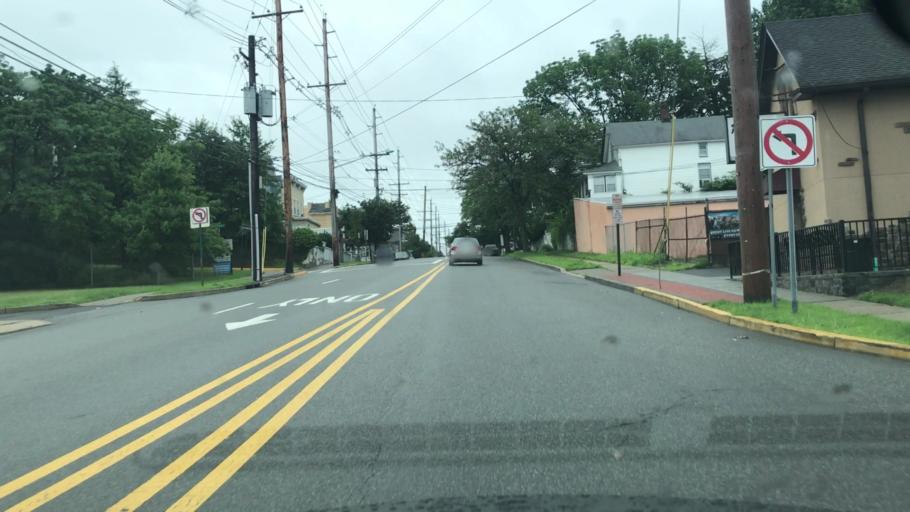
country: US
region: New Jersey
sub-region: Bergen County
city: East Rutherford
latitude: 40.8404
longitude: -74.1008
